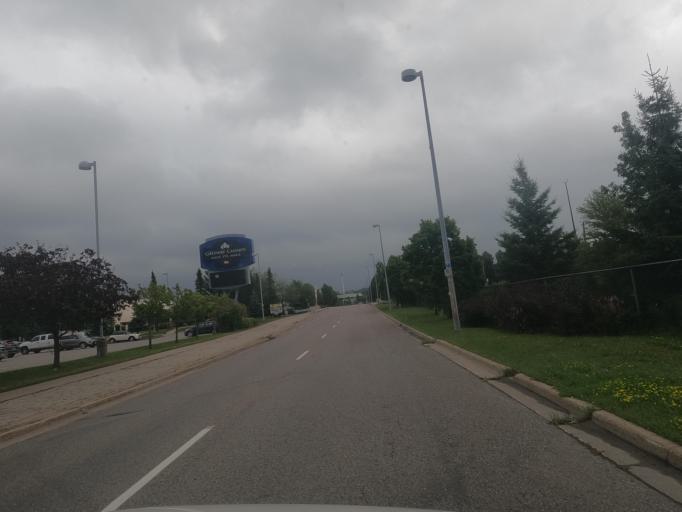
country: CA
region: Ontario
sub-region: Algoma
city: Sault Ste. Marie
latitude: 46.5169
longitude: -84.3460
